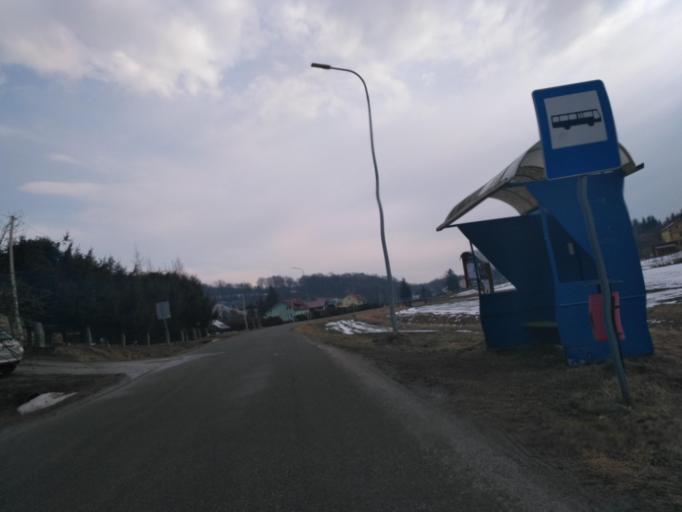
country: PL
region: Subcarpathian Voivodeship
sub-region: Powiat brzozowski
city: Grabownica Starzenska
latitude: 49.6426
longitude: 22.1018
